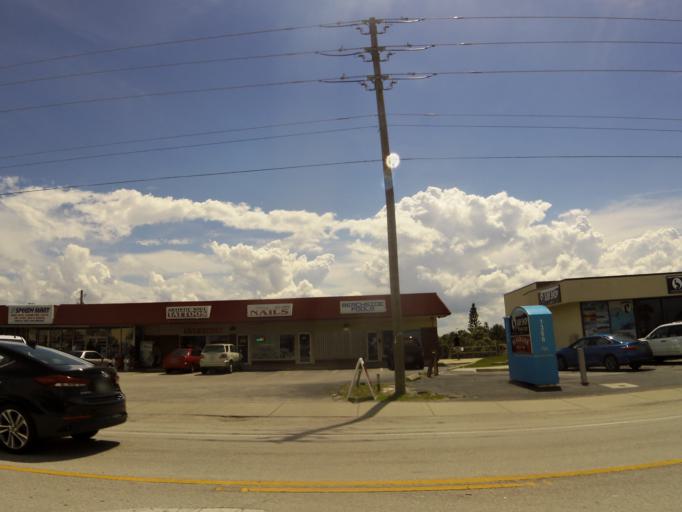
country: US
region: Florida
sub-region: Volusia County
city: Ormond-by-the-Sea
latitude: 29.3264
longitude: -81.0568
